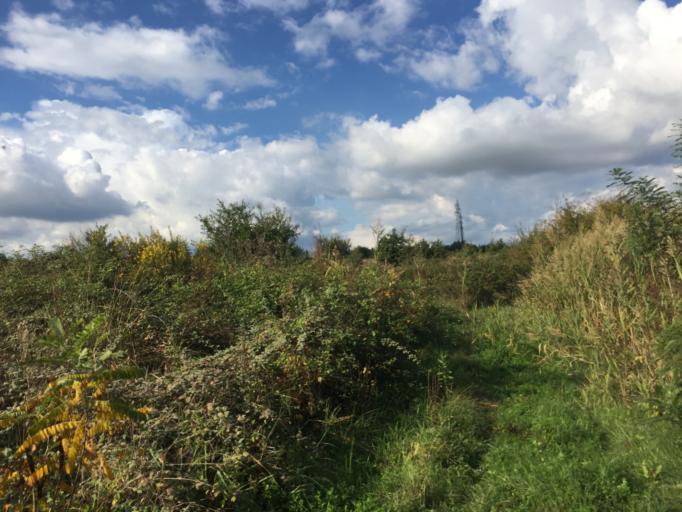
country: IT
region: Tuscany
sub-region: Provincia di Lucca
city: Spianate
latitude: 43.8268
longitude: 10.7019
